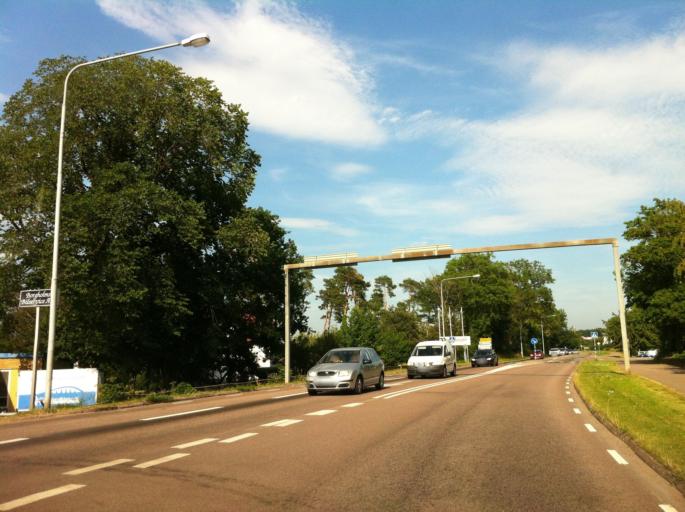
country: SE
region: Kalmar
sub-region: Borgholms Kommun
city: Borgholm
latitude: 56.8736
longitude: 16.6683
